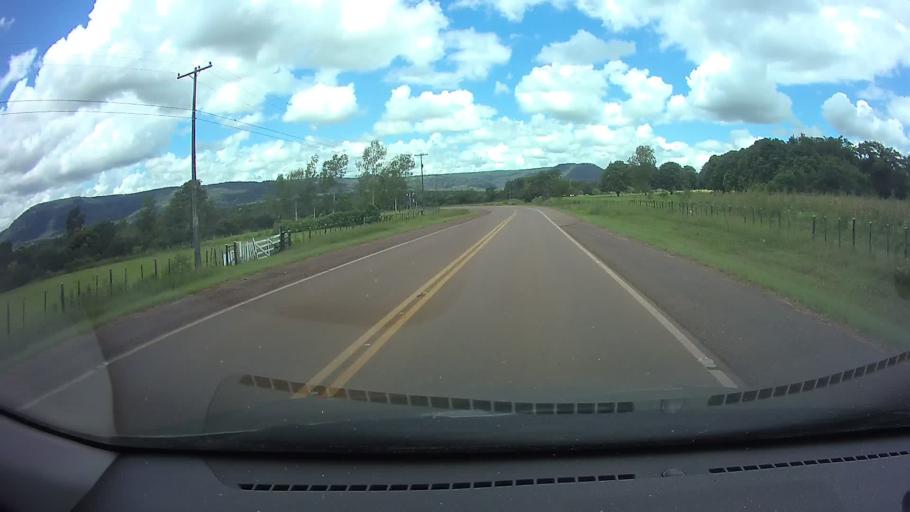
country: PY
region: Paraguari
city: La Colmena
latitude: -25.8944
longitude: -56.7997
